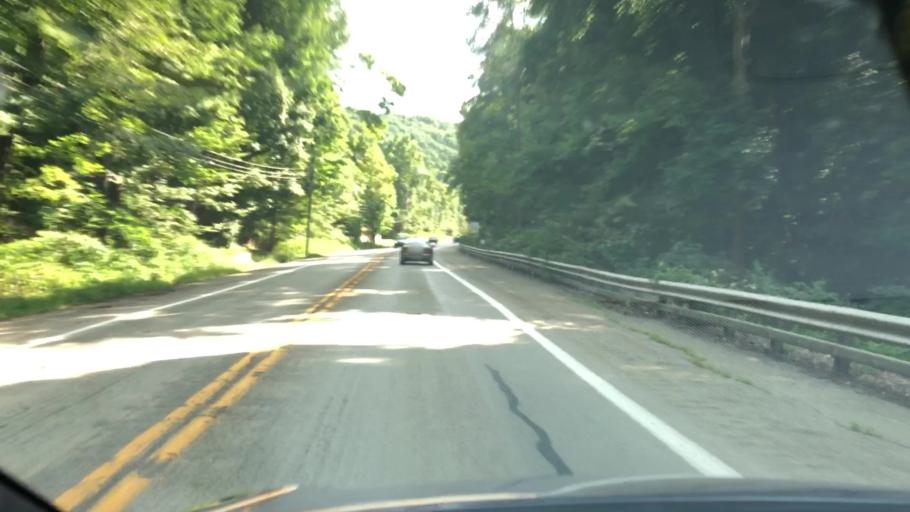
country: US
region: Pennsylvania
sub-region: Allegheny County
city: Pitcairn
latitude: 40.4095
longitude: -79.7608
